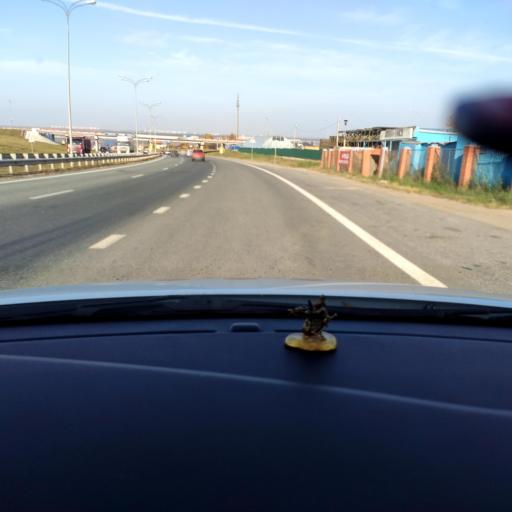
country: RU
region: Tatarstan
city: Osinovo
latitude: 55.7714
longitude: 48.8372
